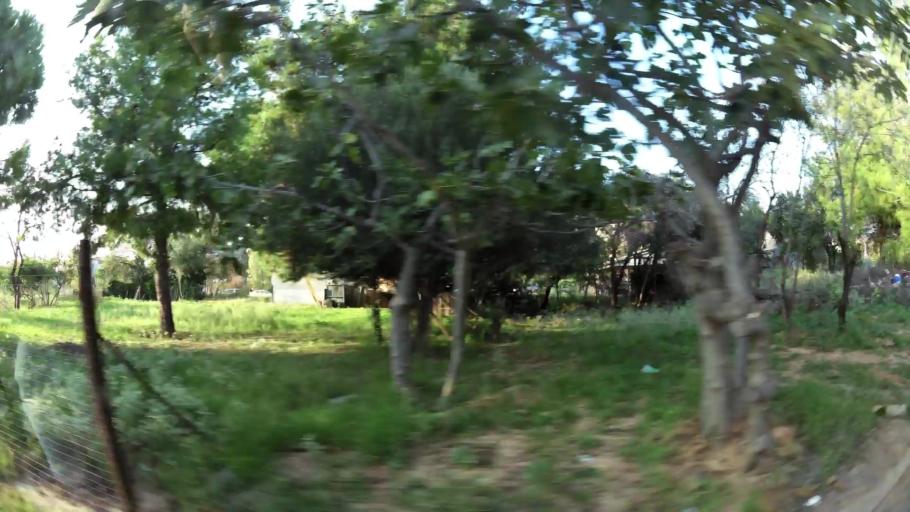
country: GR
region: Attica
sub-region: Nomarchia Athinas
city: Agia Paraskevi
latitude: 38.0226
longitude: 23.8284
